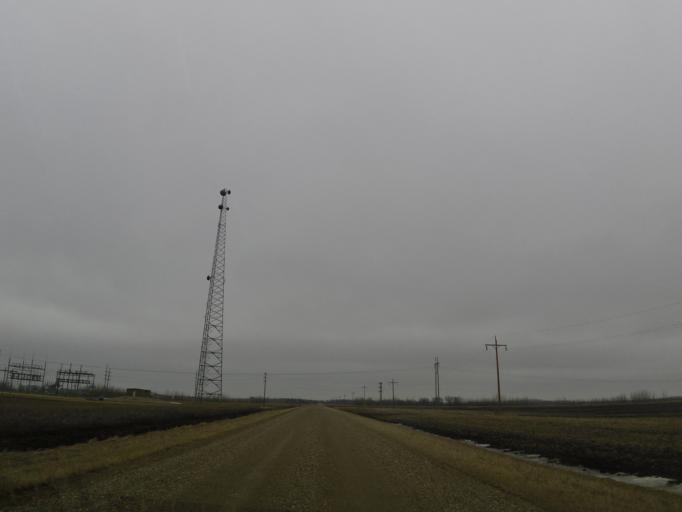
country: US
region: North Dakota
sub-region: Walsh County
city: Grafton
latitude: 48.3531
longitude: -97.1714
